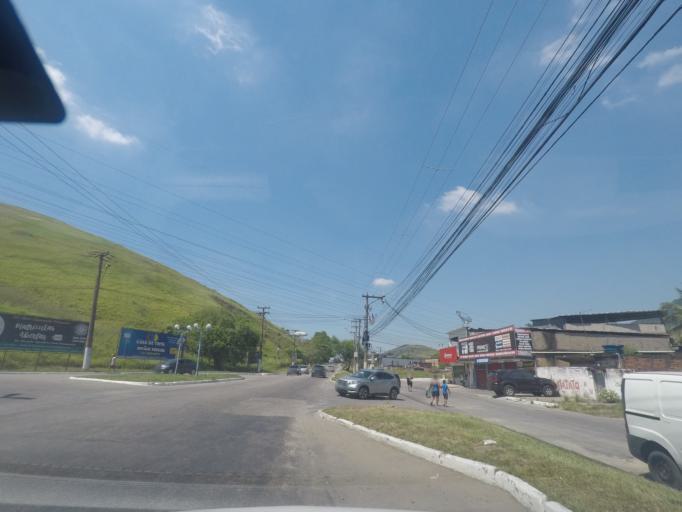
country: BR
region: Rio de Janeiro
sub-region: Petropolis
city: Petropolis
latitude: -22.6029
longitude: -43.1902
